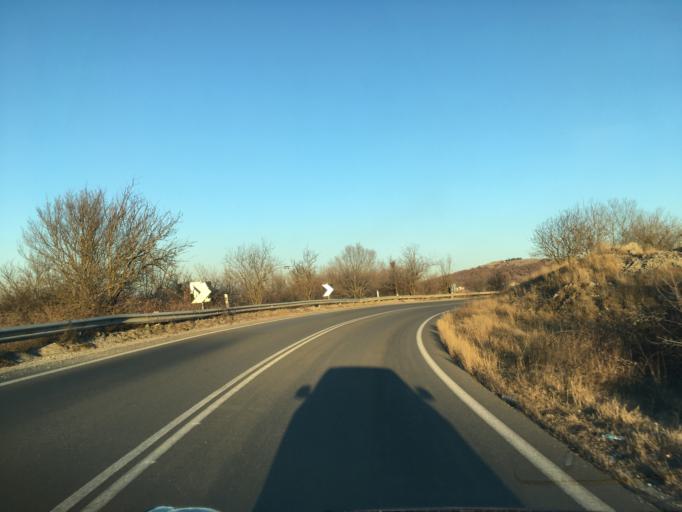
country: GR
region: West Macedonia
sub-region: Nomos Kozanis
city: Koila
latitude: 40.3255
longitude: 21.7798
